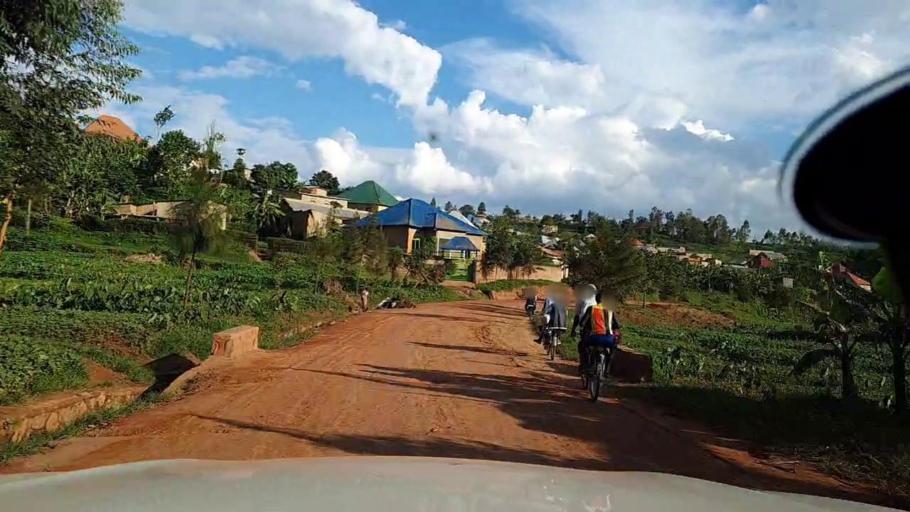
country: RW
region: Kigali
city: Kigali
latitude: -1.8948
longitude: 29.9643
